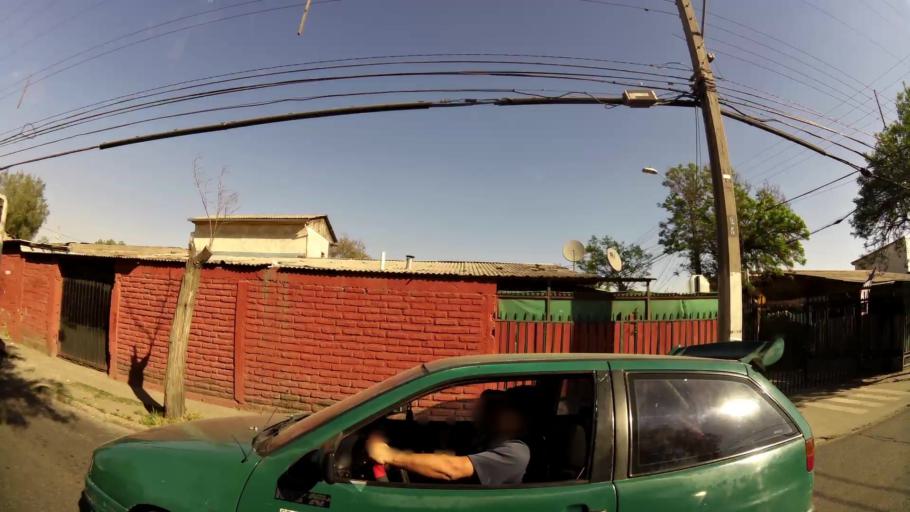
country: CL
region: Santiago Metropolitan
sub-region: Provincia de Santiago
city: La Pintana
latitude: -33.5615
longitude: -70.6058
